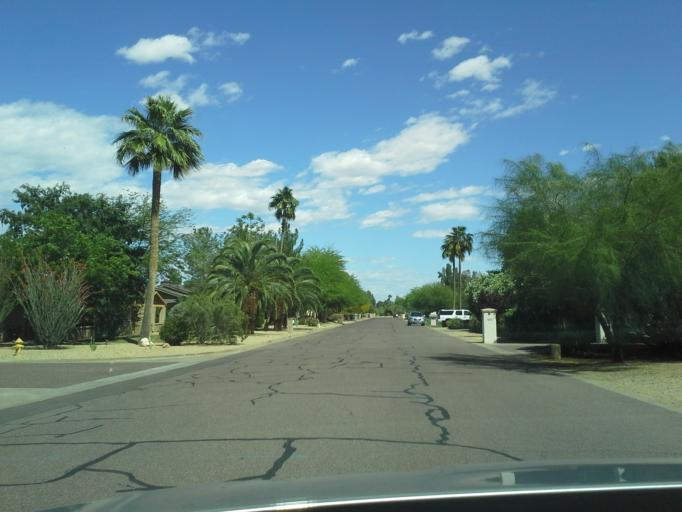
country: US
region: Arizona
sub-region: Maricopa County
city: Paradise Valley
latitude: 33.5749
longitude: -111.9468
